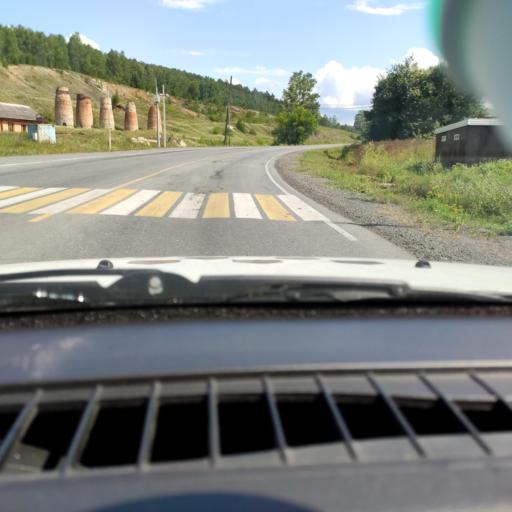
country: RU
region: Chelyabinsk
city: Mezhevoy
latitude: 55.1563
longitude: 58.8270
